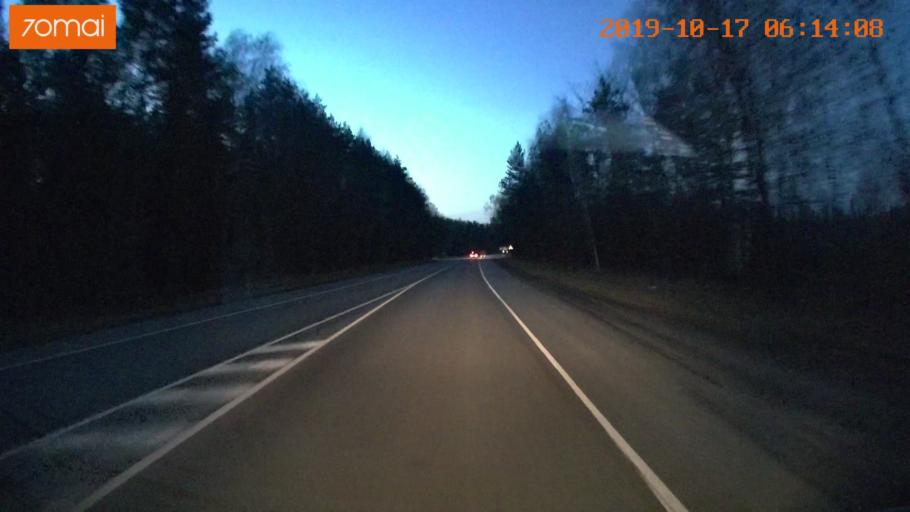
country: RU
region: Ivanovo
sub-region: Gorod Ivanovo
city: Ivanovo
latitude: 56.8897
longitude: 40.9412
